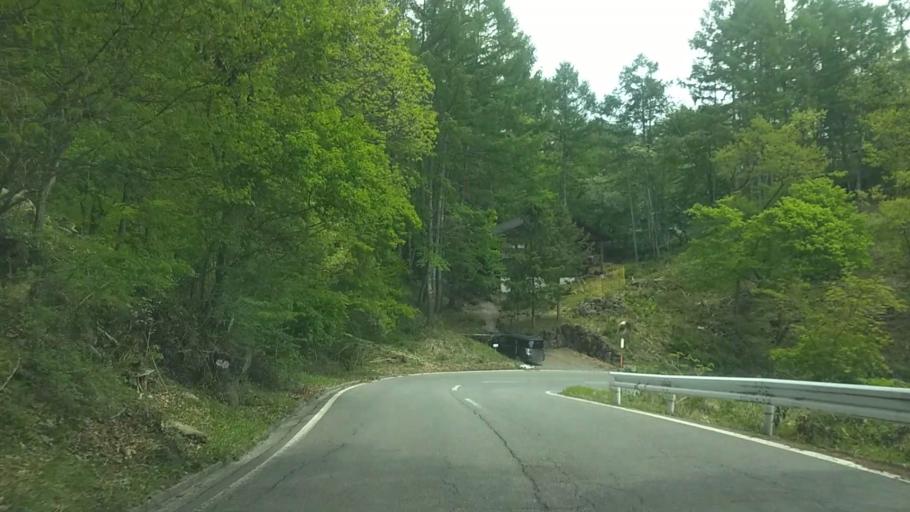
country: JP
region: Nagano
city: Chino
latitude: 36.0442
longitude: 138.2690
